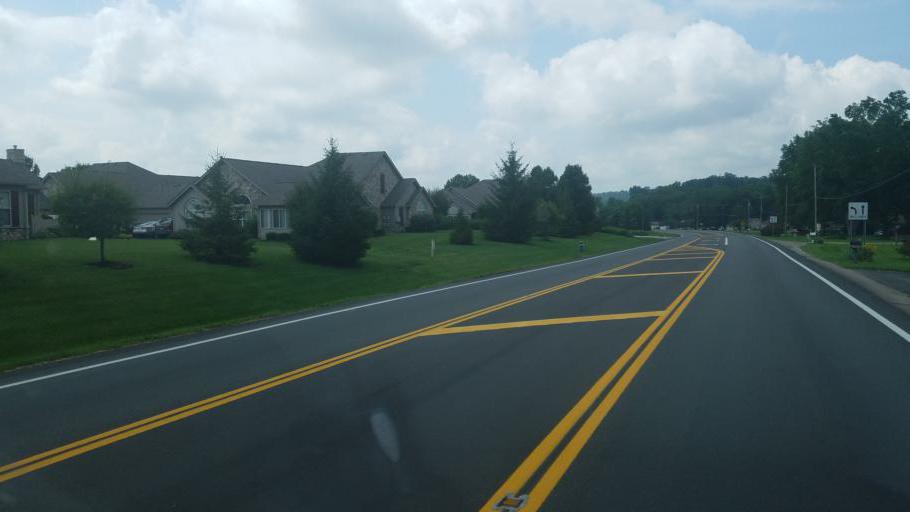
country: US
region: Ohio
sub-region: Fairfield County
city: Lancaster
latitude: 39.7516
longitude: -82.5843
